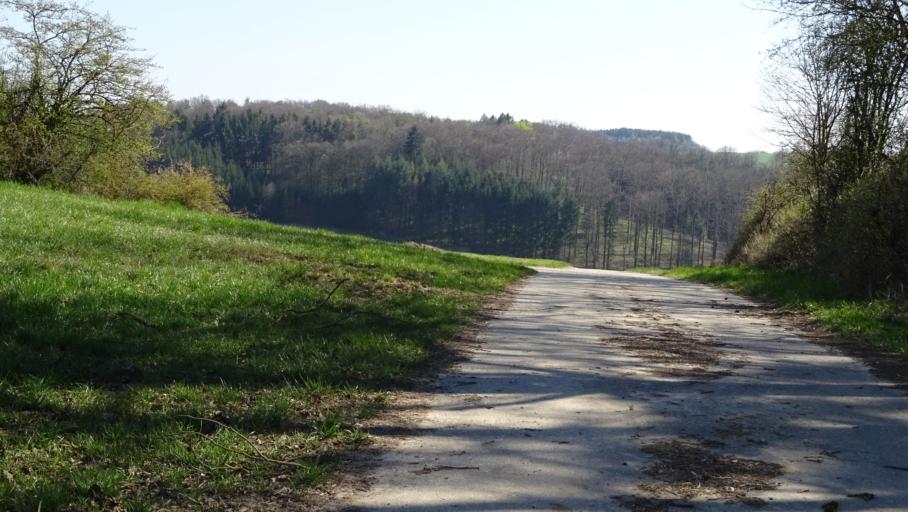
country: DE
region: Baden-Wuerttemberg
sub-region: Karlsruhe Region
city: Limbach
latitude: 49.4175
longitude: 9.2430
